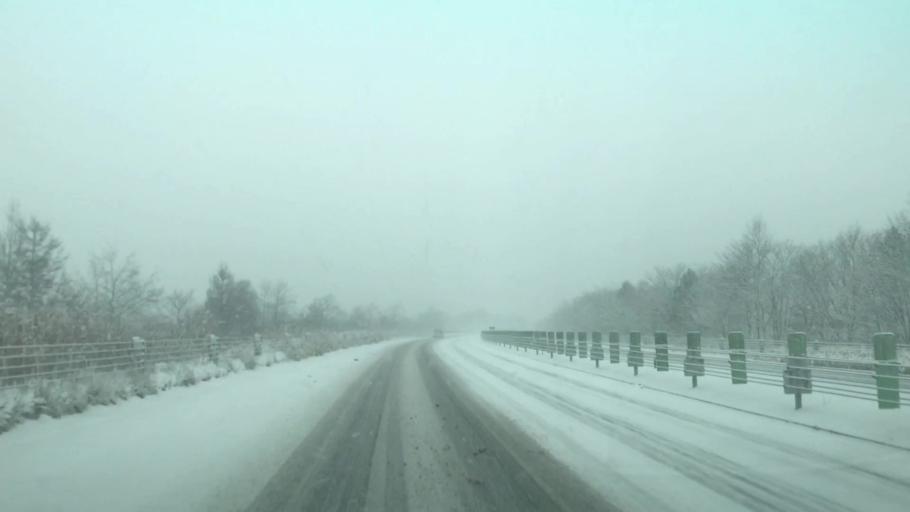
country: JP
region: Hokkaido
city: Shiraoi
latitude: 42.5041
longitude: 141.2675
